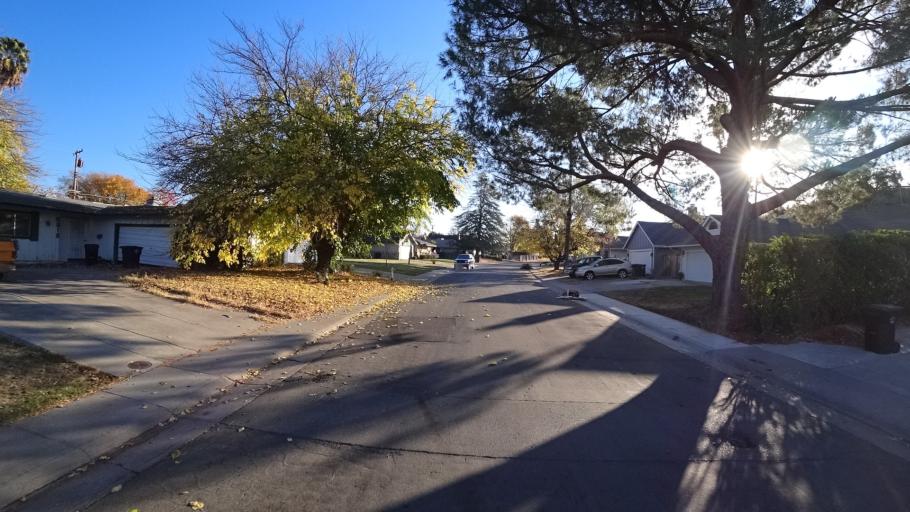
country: US
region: California
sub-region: Sacramento County
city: Citrus Heights
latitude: 38.6758
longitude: -121.3027
